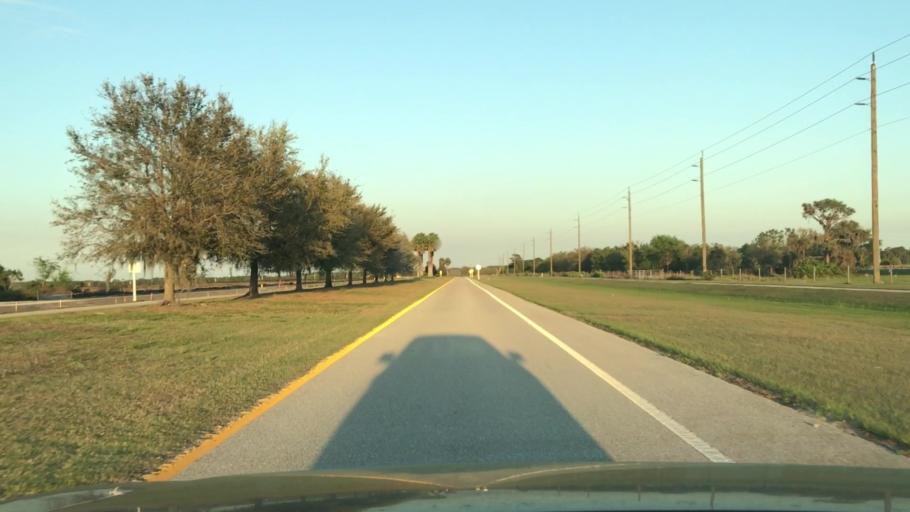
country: US
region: Florida
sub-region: Sarasota County
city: The Meadows
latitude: 27.3859
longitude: -82.3687
